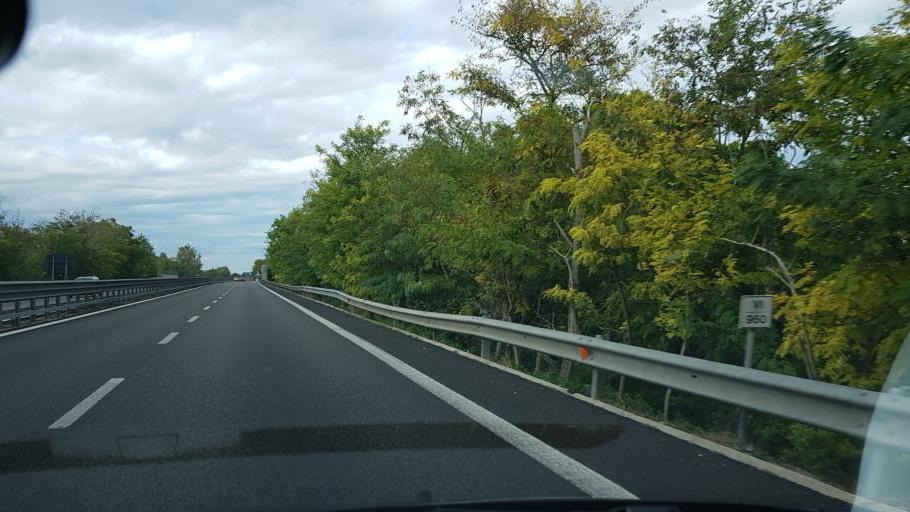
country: IT
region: Apulia
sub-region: Provincia di Lecce
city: Cavallino
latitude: 40.3162
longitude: 18.1889
